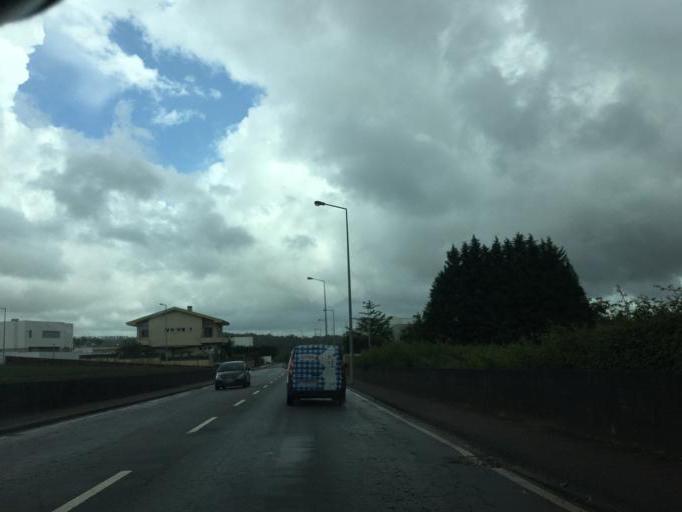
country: PT
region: Porto
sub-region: Maia
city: Nogueira
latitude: 41.2544
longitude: -8.5940
